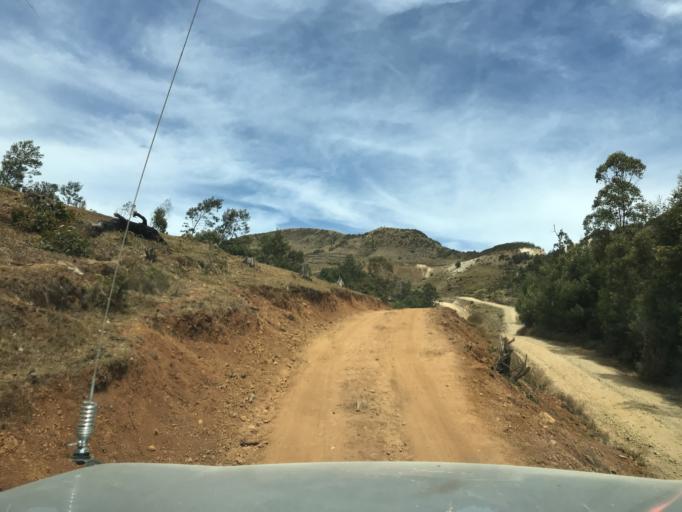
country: TL
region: Ainaro
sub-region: Ainaro
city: Ainaro
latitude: -8.8744
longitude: 125.5277
